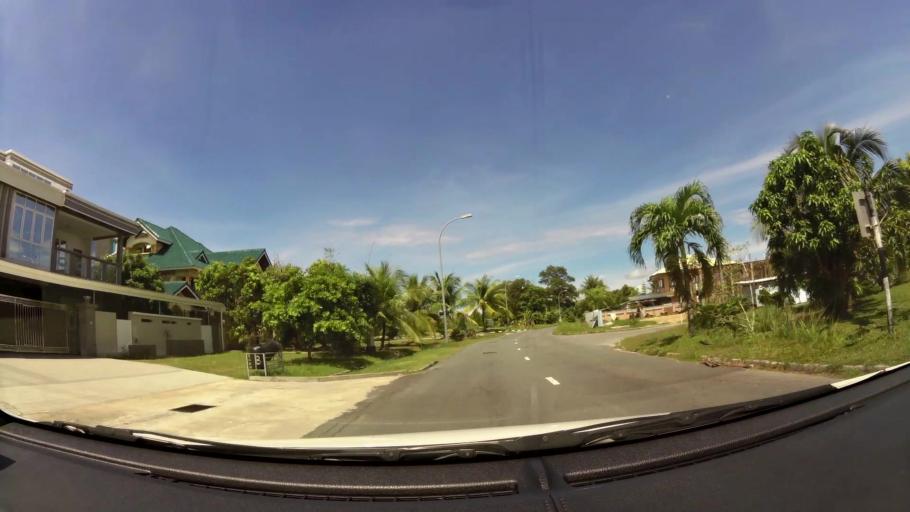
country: BN
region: Belait
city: Kuala Belait
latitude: 4.5884
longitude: 114.2232
